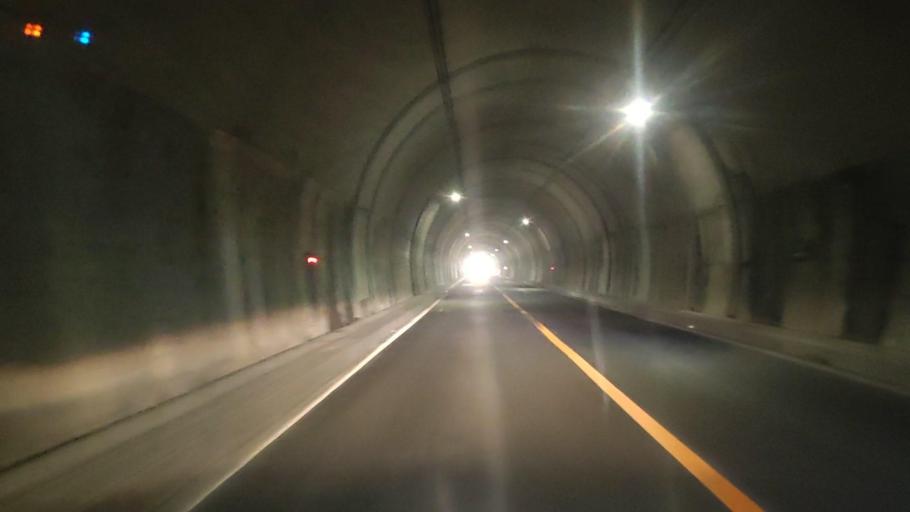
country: JP
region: Oita
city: Saiki
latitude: 32.8836
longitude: 131.9462
